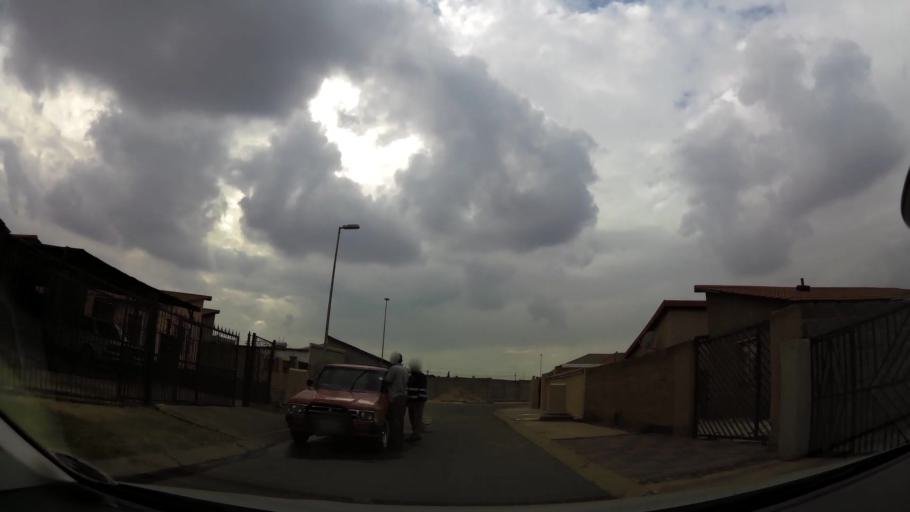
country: ZA
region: Gauteng
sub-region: City of Johannesburg Metropolitan Municipality
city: Soweto
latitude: -26.2582
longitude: 27.8577
